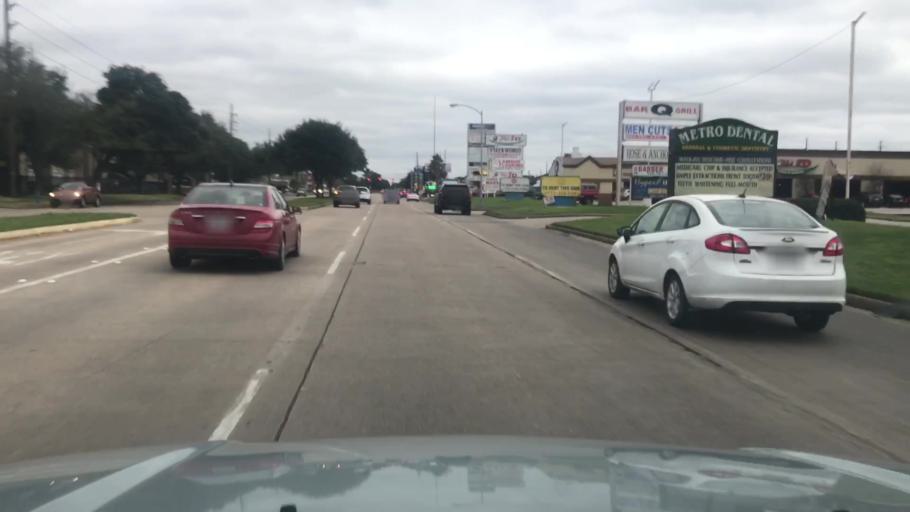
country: US
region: Texas
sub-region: Fort Bend County
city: Cinco Ranch
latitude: 29.7674
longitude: -95.7517
